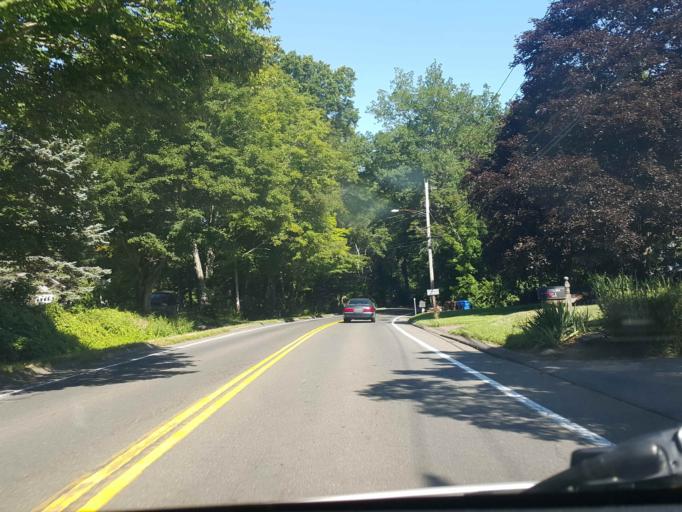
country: US
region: Connecticut
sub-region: New Haven County
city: North Branford
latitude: 41.3126
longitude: -72.7471
